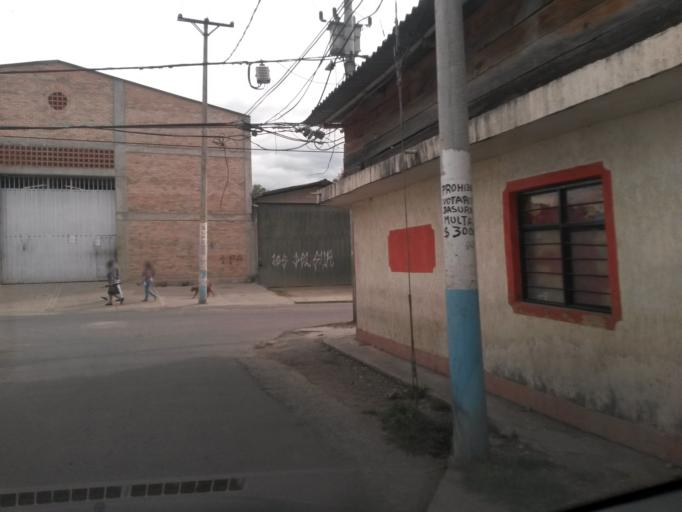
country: CO
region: Cauca
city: Popayan
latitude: 2.4519
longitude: -76.6285
